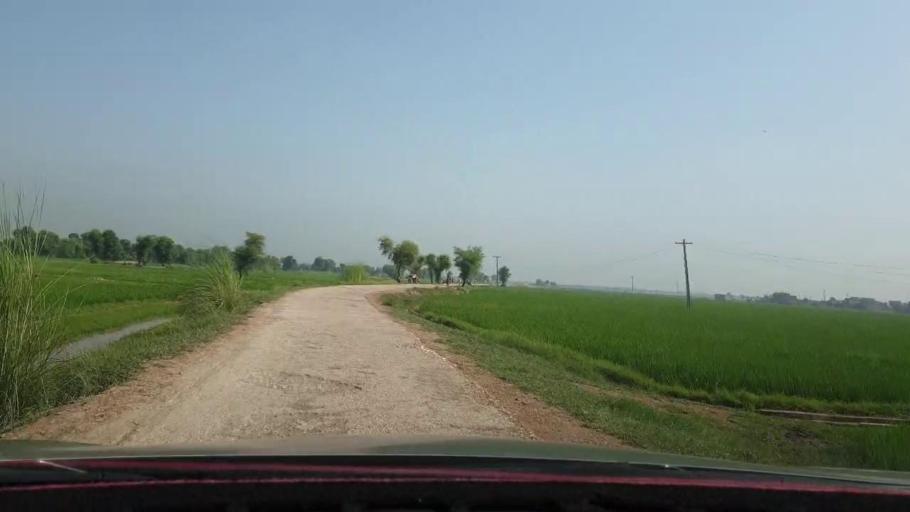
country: PK
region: Sindh
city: Nasirabad
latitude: 27.4908
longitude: 67.9276
